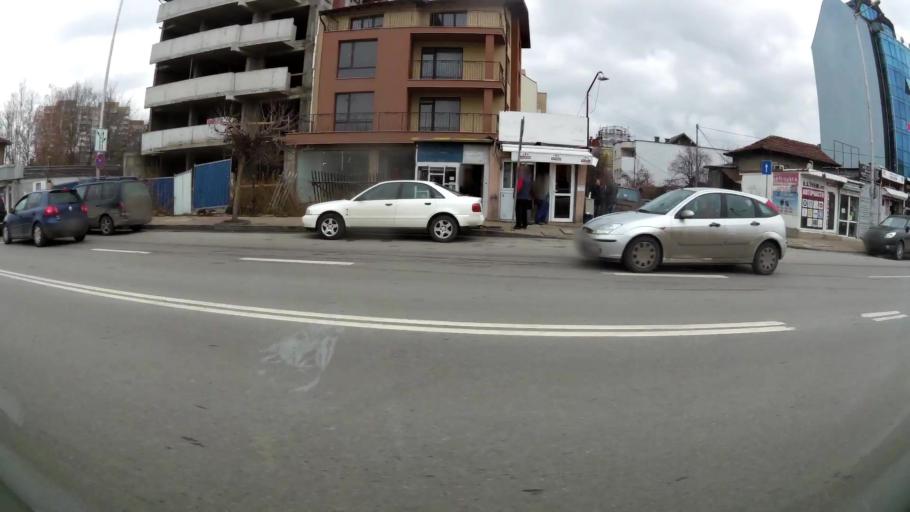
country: BG
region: Sofia-Capital
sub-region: Stolichna Obshtina
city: Sofia
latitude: 42.7317
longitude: 23.2969
